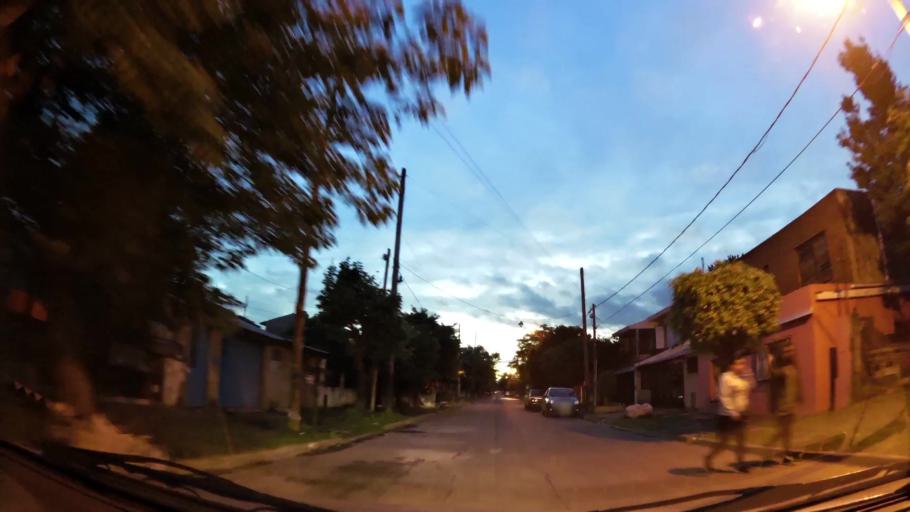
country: AR
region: Buenos Aires
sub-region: Partido de Lomas de Zamora
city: Lomas de Zamora
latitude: -34.7468
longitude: -58.3607
